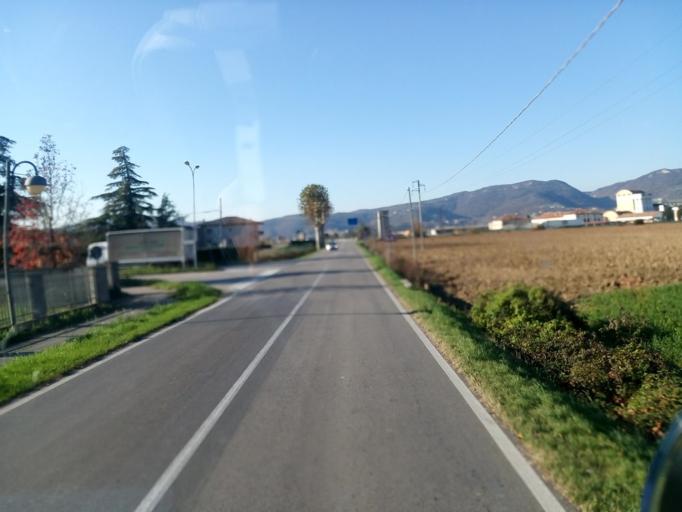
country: IT
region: Veneto
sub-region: Provincia di Vicenza
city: Ponte di Barbarano
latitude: 45.3838
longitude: 11.5743
